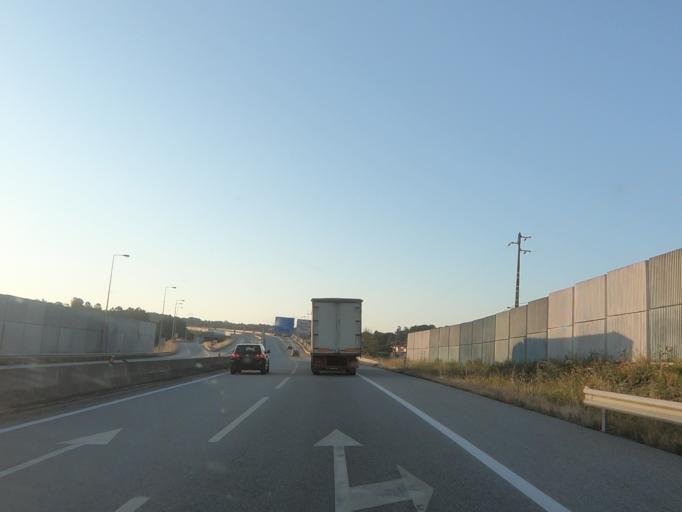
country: PT
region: Viseu
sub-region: Viseu
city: Rio de Loba
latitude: 40.6495
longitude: -7.8607
